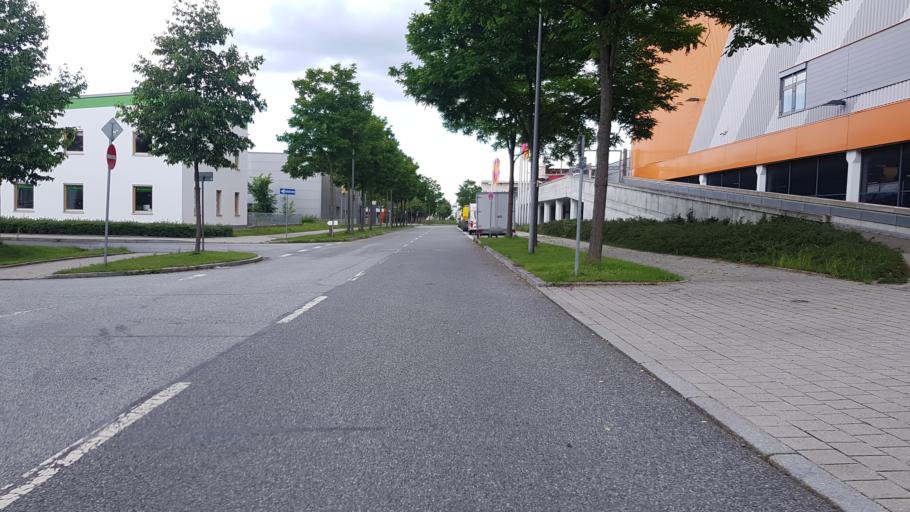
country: DE
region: Bavaria
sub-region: Upper Bavaria
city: Grafelfing
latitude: 48.1332
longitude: 11.4102
